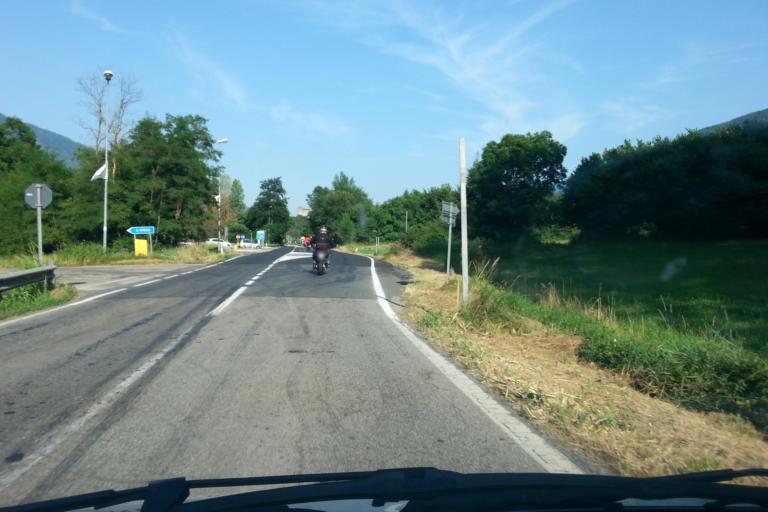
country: IT
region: Piedmont
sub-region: Provincia di Torino
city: San Giorio
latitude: 45.1309
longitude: 7.1683
